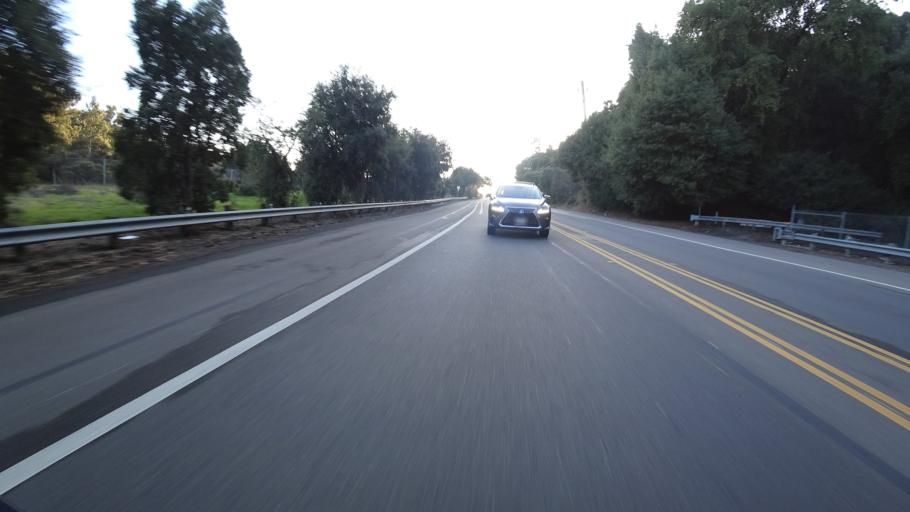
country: US
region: California
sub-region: Alameda County
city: Fairview
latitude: 37.7011
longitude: -122.0398
